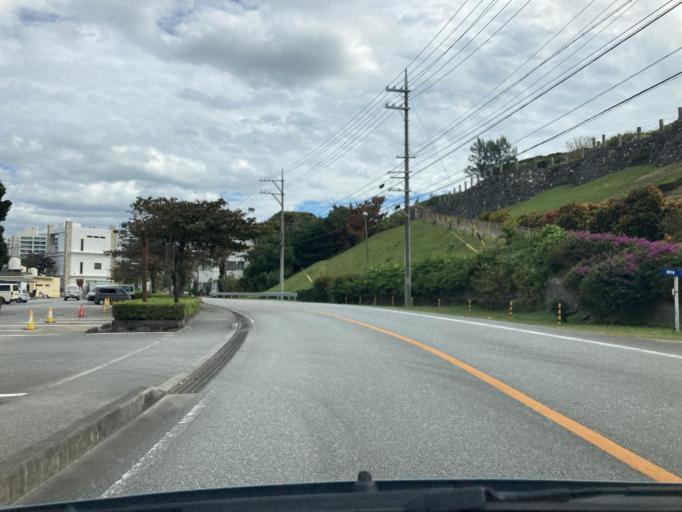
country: JP
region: Okinawa
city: Ishikawa
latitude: 26.4347
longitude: 127.7834
